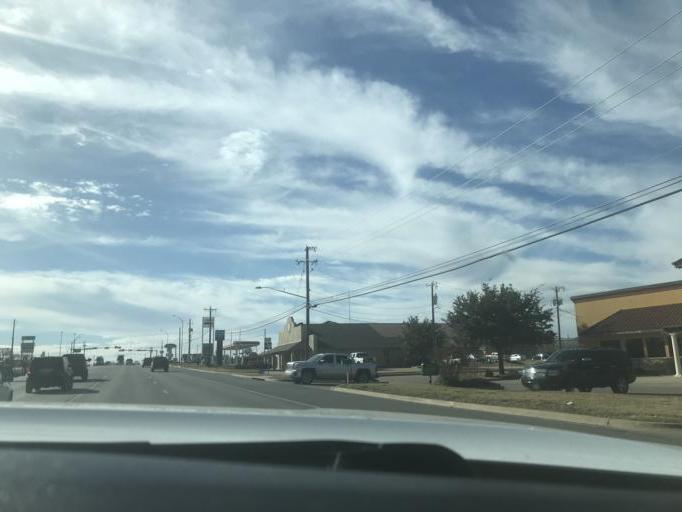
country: US
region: Texas
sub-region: Erath County
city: Stephenville
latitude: 32.2024
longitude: -98.2436
